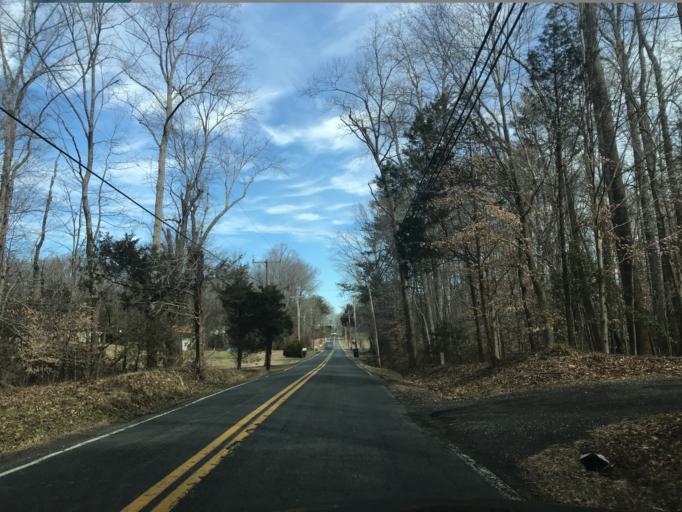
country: US
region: Maryland
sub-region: Charles County
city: La Plata
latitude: 38.5069
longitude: -76.9828
